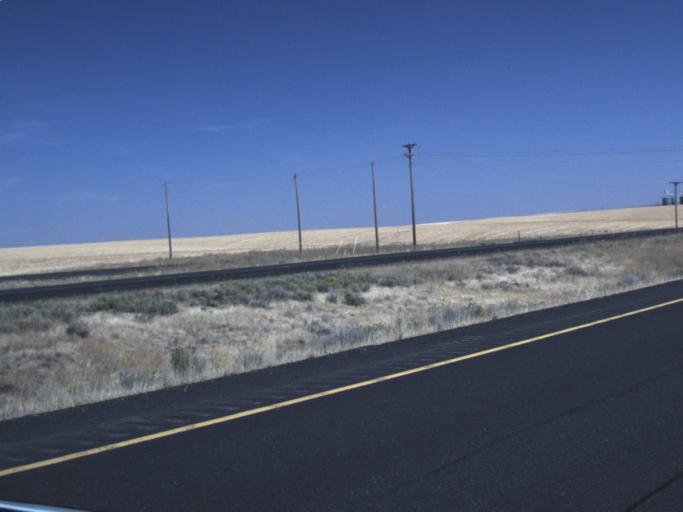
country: US
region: Washington
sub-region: Adams County
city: Ritzville
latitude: 47.0969
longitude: -118.6792
